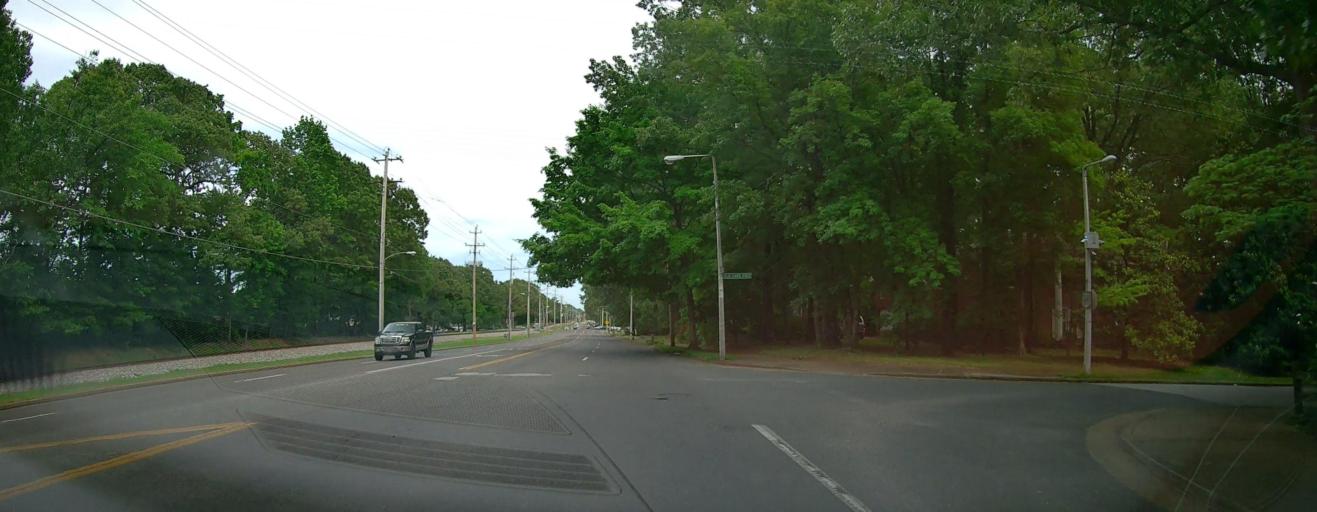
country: US
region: Tennessee
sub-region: Shelby County
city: Germantown
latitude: 35.0963
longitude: -89.8435
